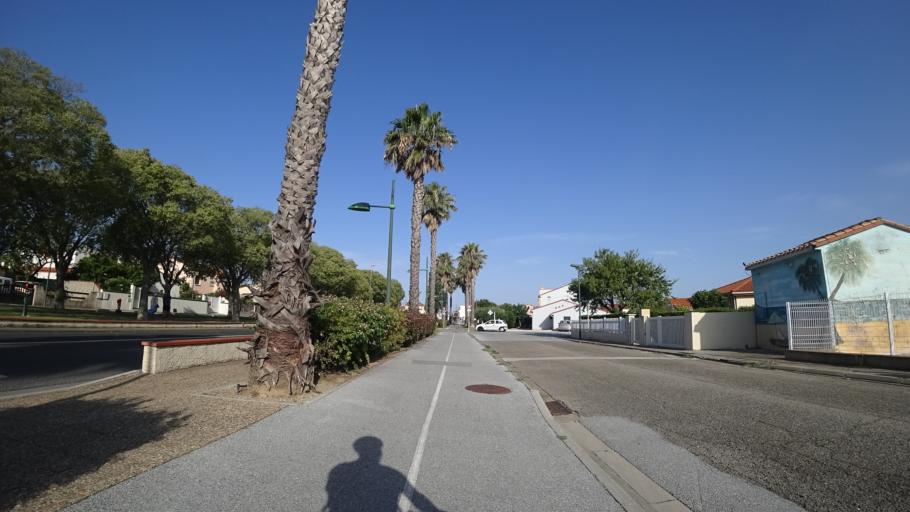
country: FR
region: Languedoc-Roussillon
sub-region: Departement des Pyrenees-Orientales
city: Saint-Laurent-de-la-Salanque
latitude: 42.7737
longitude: 2.9964
